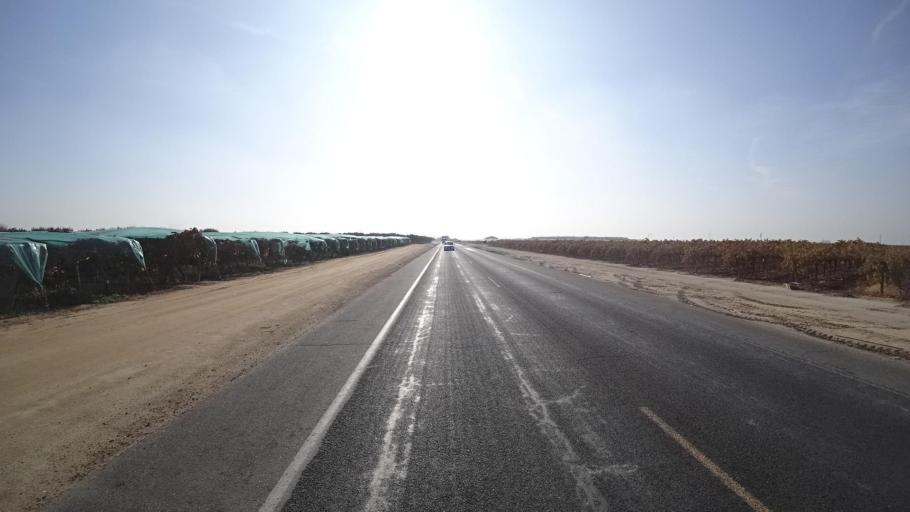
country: US
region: California
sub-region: Tulare County
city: Richgrove
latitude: 35.7516
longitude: -119.1389
